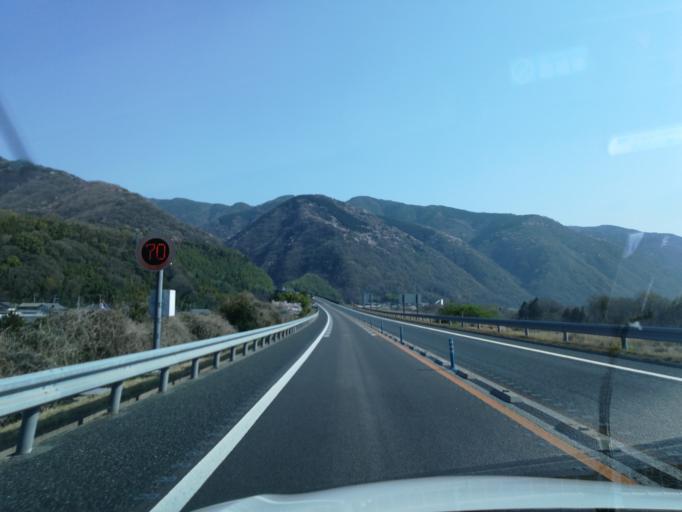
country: JP
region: Tokushima
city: Ikedacho
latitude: 34.0431
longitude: 133.9111
